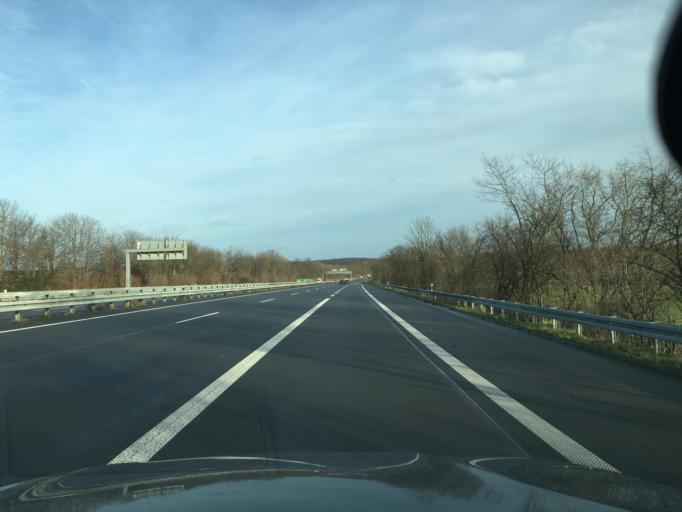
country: DE
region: North Rhine-Westphalia
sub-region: Regierungsbezirk Koln
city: Weilerswist
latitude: 50.7715
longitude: 6.8262
